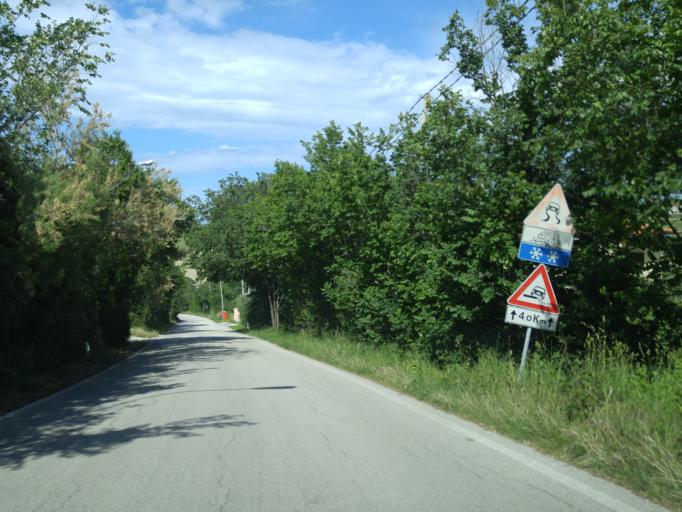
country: IT
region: The Marches
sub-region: Provincia di Pesaro e Urbino
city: Bellocchi
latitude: 43.7798
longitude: 13.0383
